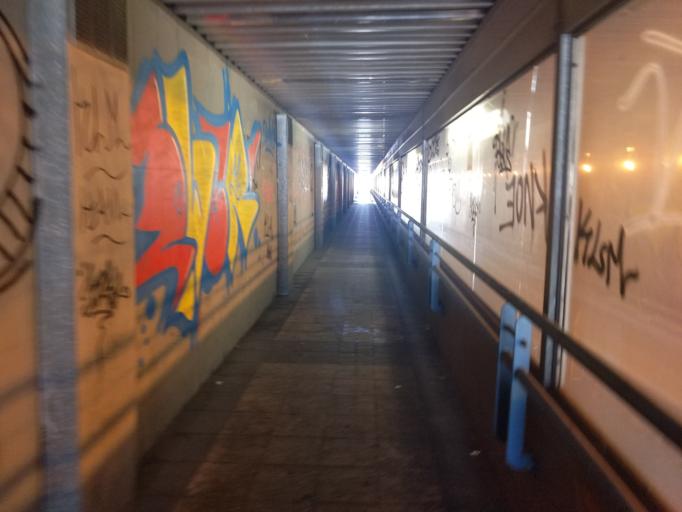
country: IT
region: Apulia
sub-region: Provincia di Bari
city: Bari
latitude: 41.1158
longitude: 16.8526
